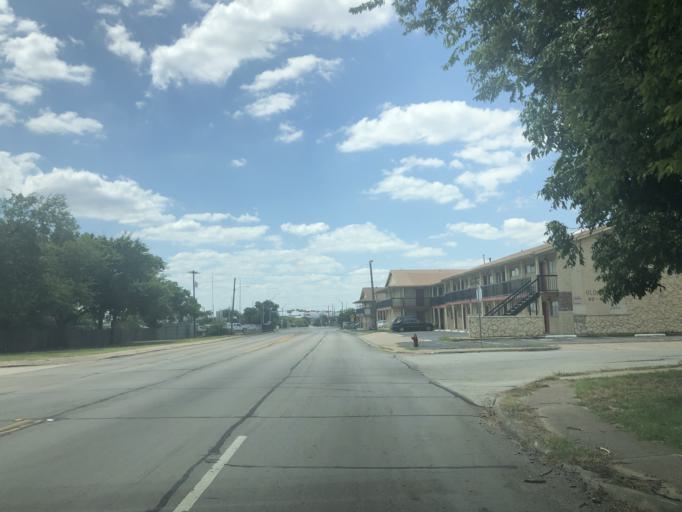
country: US
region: Texas
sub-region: Dallas County
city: Grand Prairie
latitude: 32.7424
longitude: -97.0292
